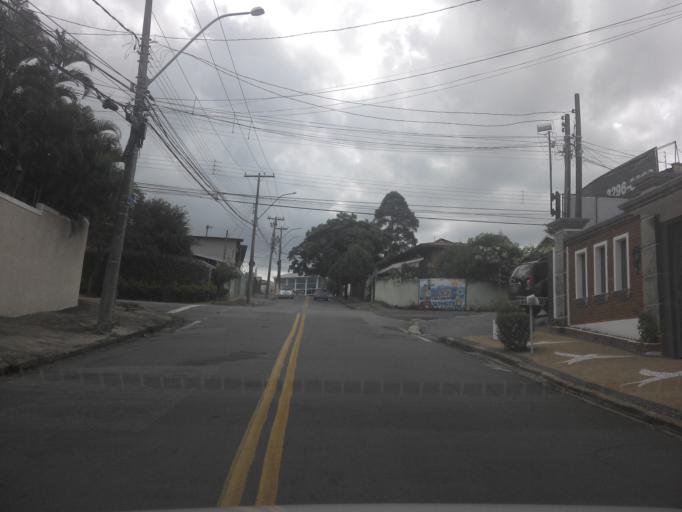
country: BR
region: Sao Paulo
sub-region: Campinas
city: Campinas
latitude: -22.8685
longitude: -47.0388
